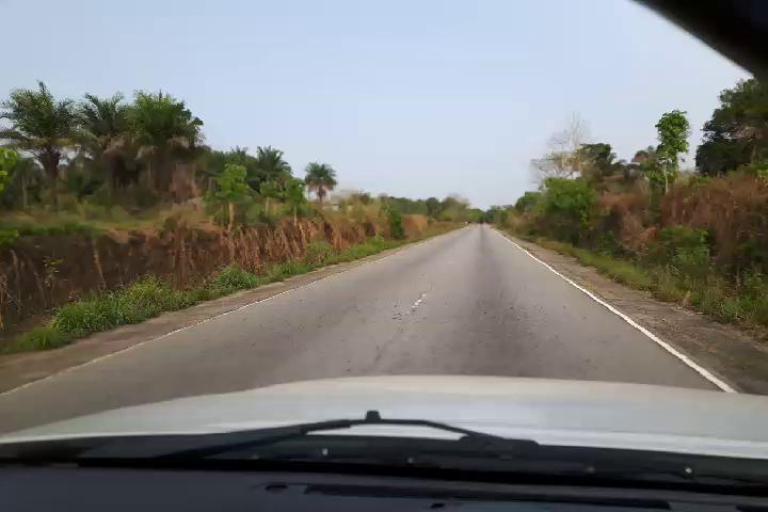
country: SL
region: Eastern Province
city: Blama
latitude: 7.9389
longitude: -11.4933
